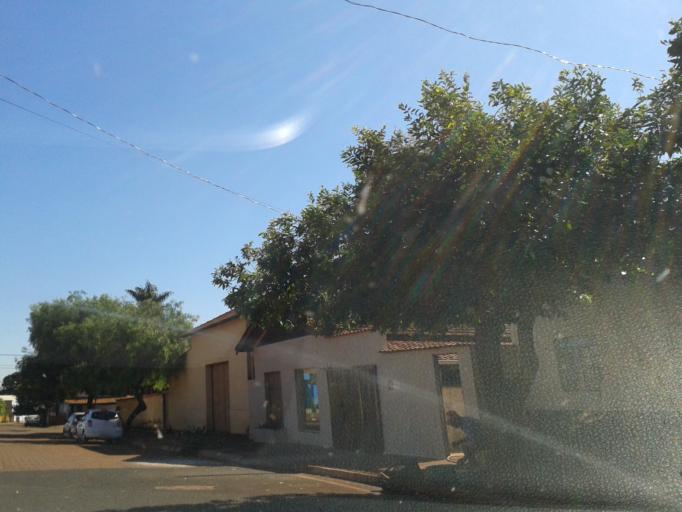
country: BR
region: Minas Gerais
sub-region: Centralina
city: Centralina
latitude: -18.5876
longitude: -49.1934
